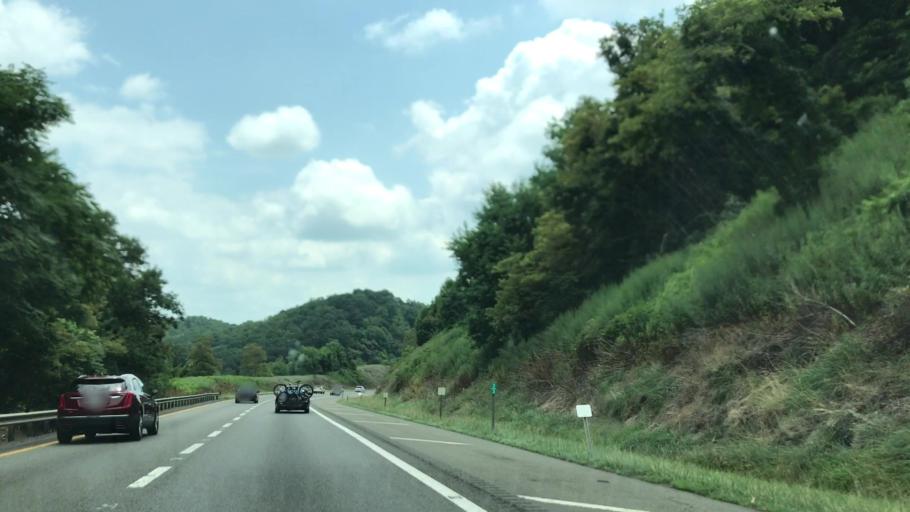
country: US
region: Virginia
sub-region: Carroll County
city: Cana
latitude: 36.6074
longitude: -80.7371
